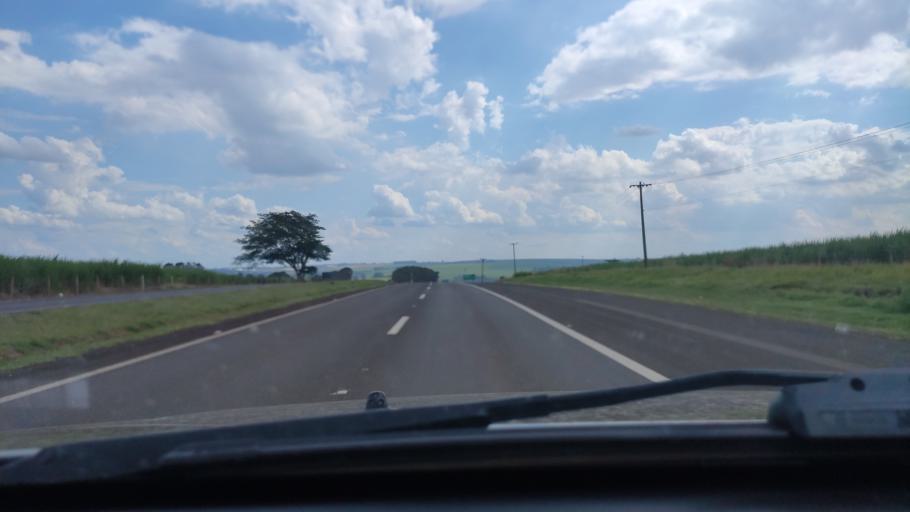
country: BR
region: Sao Paulo
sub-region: Pederneiras
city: Pederneiras
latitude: -22.3110
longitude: -48.7125
